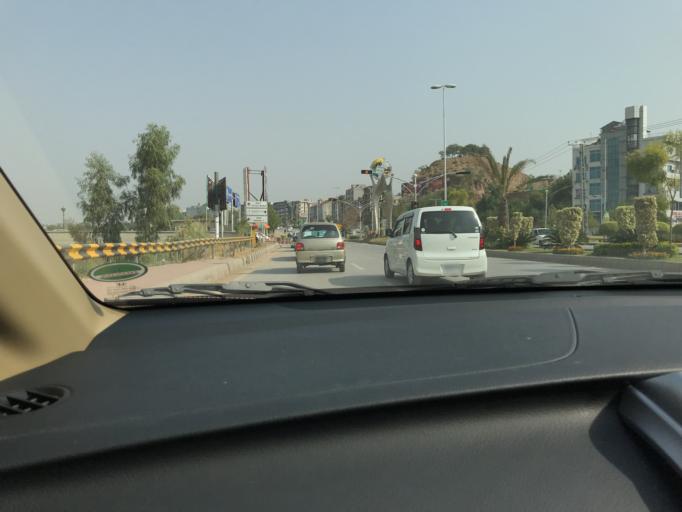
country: PK
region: Punjab
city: Rawalpindi
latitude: 33.5218
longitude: 73.1033
